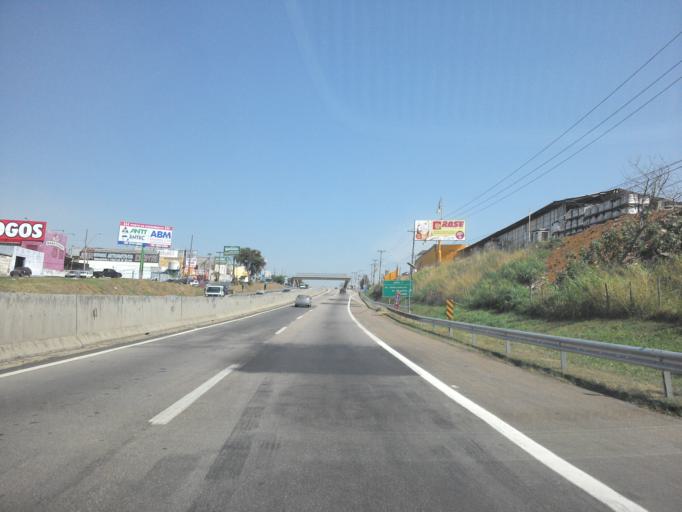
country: BR
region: Sao Paulo
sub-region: Hortolandia
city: Hortolandia
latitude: -22.8920
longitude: -47.1715
